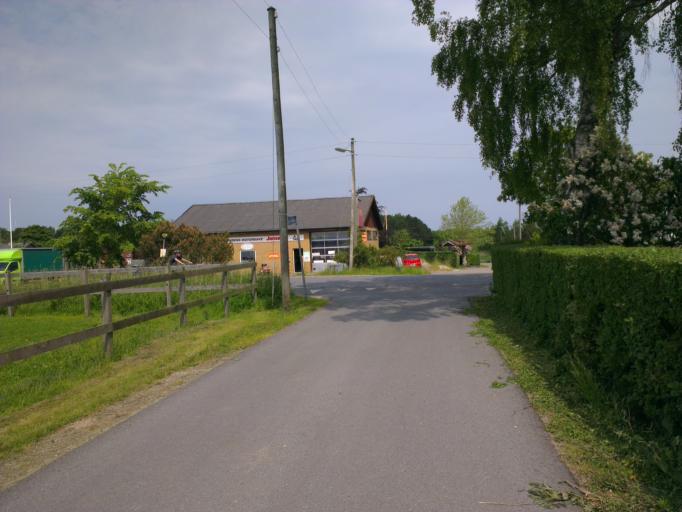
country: DK
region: Capital Region
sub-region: Frederikssund Kommune
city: Jaegerspris
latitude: 55.8176
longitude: 12.0069
